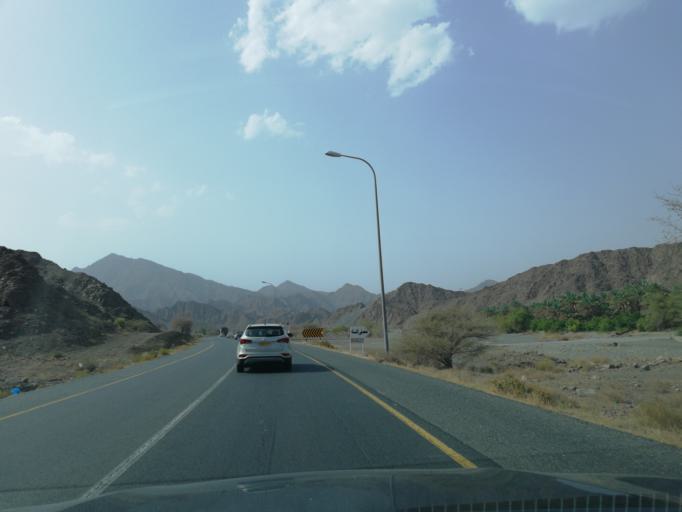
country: OM
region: Muhafazat ad Dakhiliyah
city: Sufalat Sama'il
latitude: 23.2157
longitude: 58.0766
